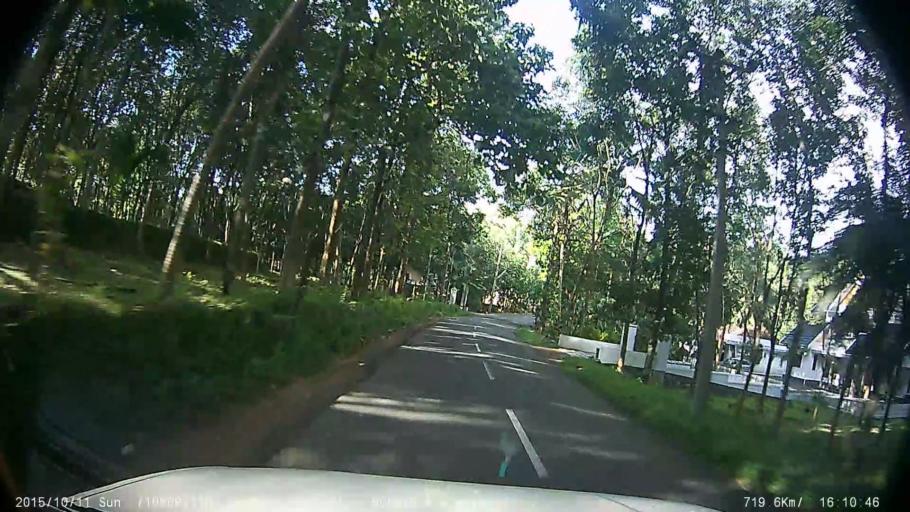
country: IN
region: Kerala
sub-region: Kottayam
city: Palackattumala
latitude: 9.7041
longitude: 76.6086
